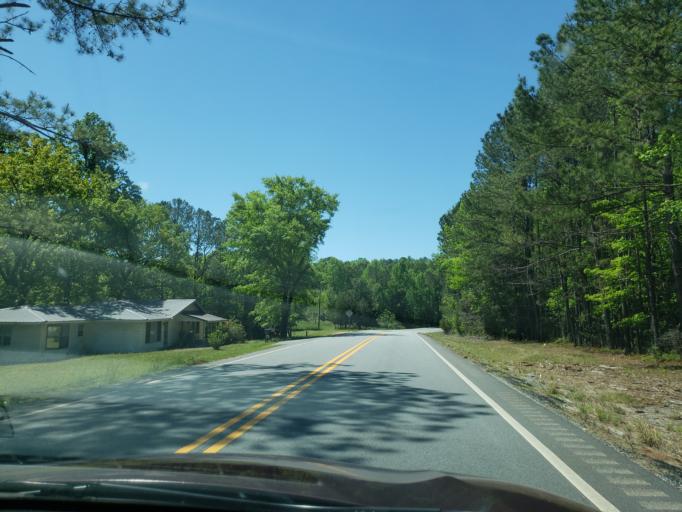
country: US
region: Alabama
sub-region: Elmore County
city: Tallassee
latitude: 32.6682
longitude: -85.7944
